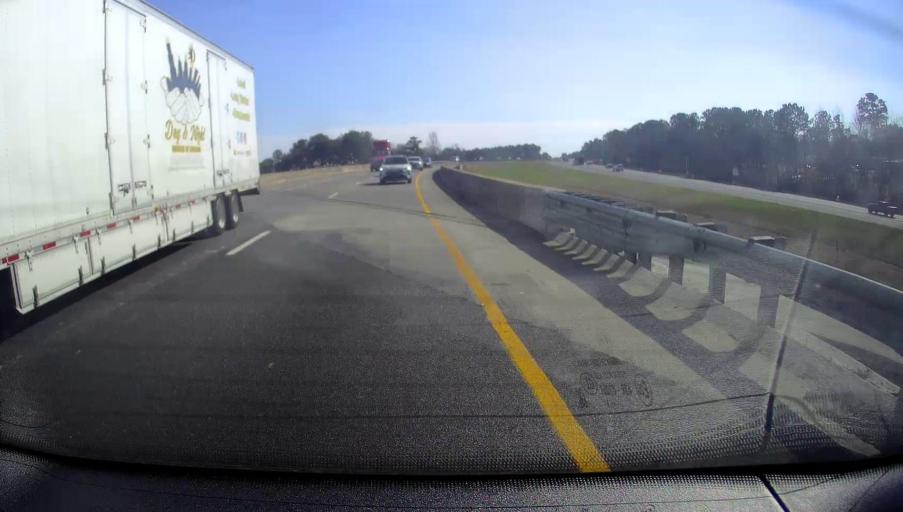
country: US
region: Georgia
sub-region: Monroe County
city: Forsyth
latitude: 32.9573
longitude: -83.8166
